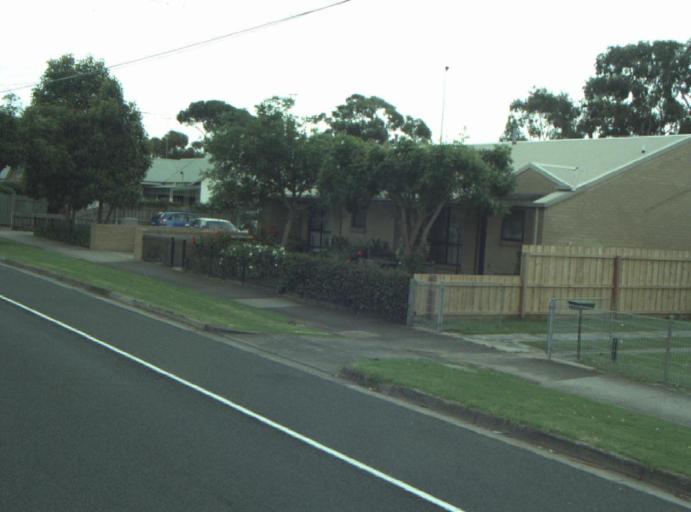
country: AU
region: Victoria
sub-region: Greater Geelong
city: East Geelong
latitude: -38.1673
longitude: 144.3751
